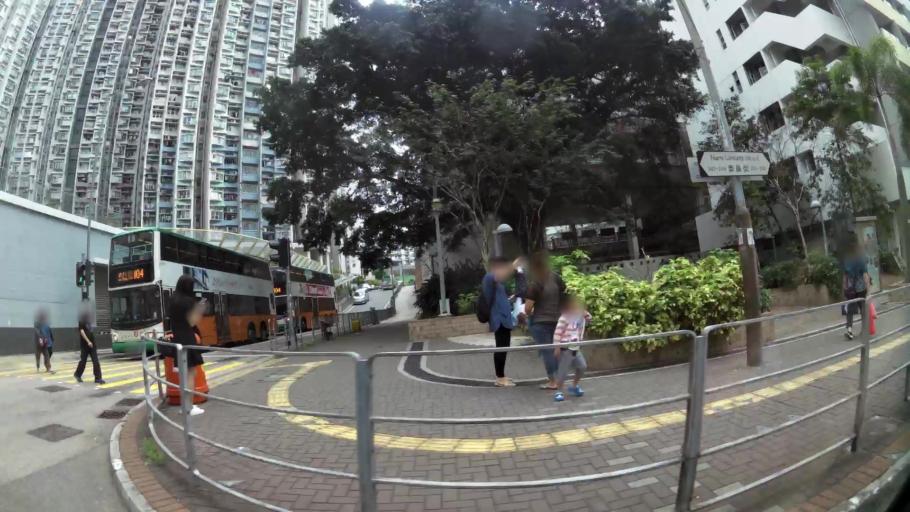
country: HK
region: Sham Shui Po
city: Sham Shui Po
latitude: 22.3338
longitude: 114.1674
